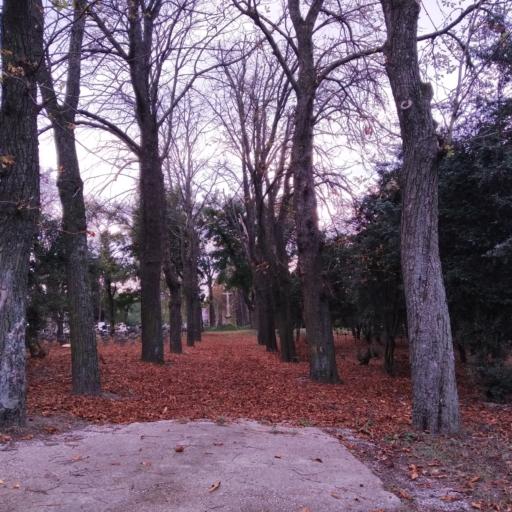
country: HU
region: Komarom-Esztergom
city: Esztergom
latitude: 47.8080
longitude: 18.7393
